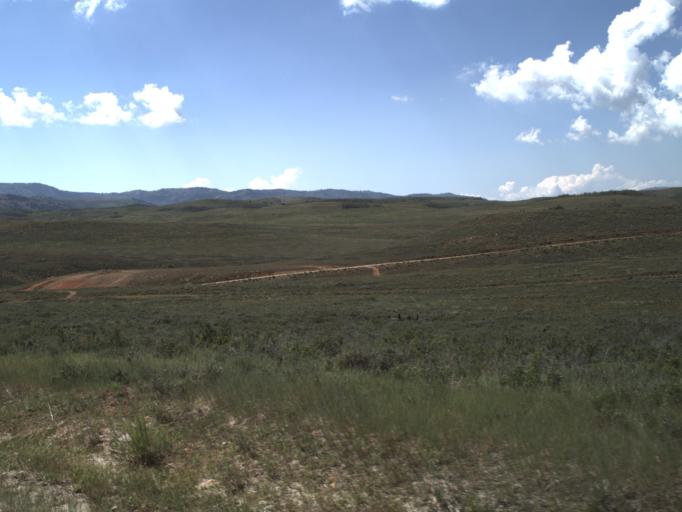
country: US
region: Utah
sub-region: Weber County
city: Wolf Creek
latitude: 41.4086
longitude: -111.5866
